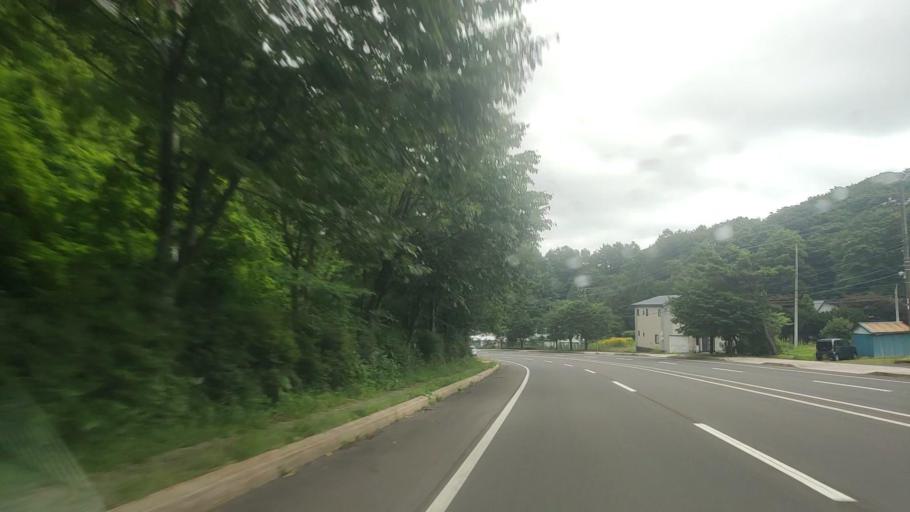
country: JP
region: Hokkaido
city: Shiraoi
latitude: 42.4700
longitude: 141.1525
